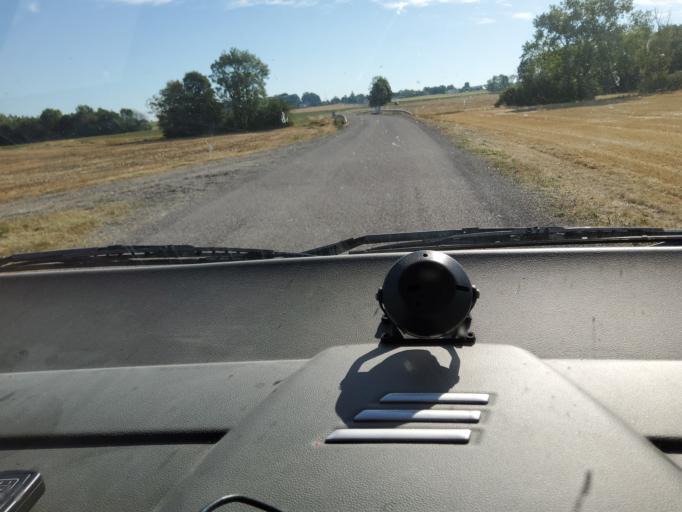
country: FR
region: Bourgogne
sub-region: Departement de la Cote-d'Or
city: Brazey-en-Plaine
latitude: 47.1379
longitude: 5.2293
